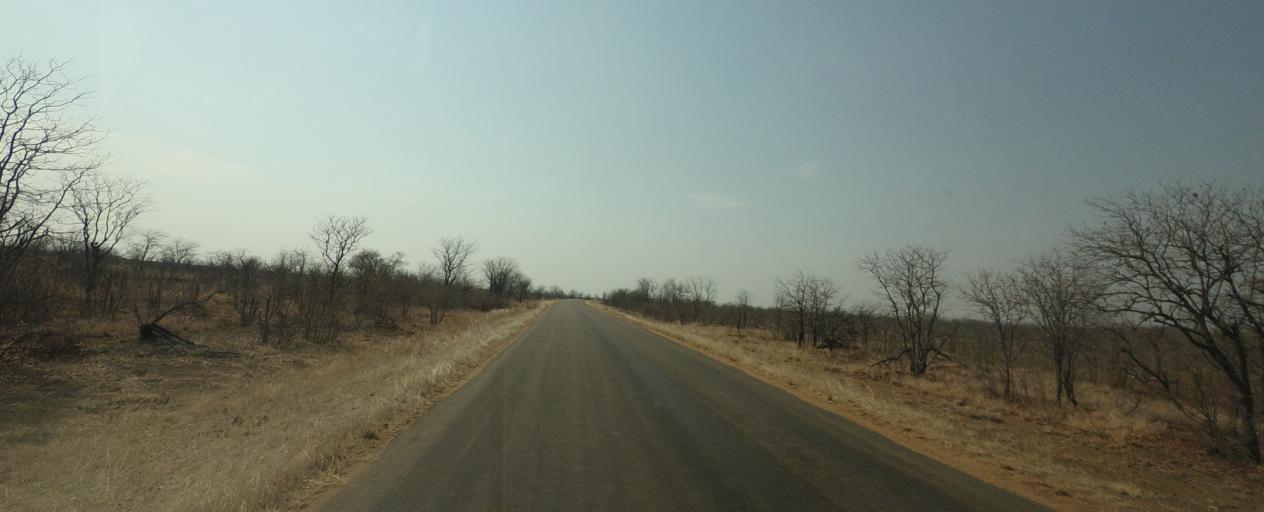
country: ZA
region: Limpopo
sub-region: Mopani District Municipality
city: Phalaborwa
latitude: -23.9420
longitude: 31.6132
